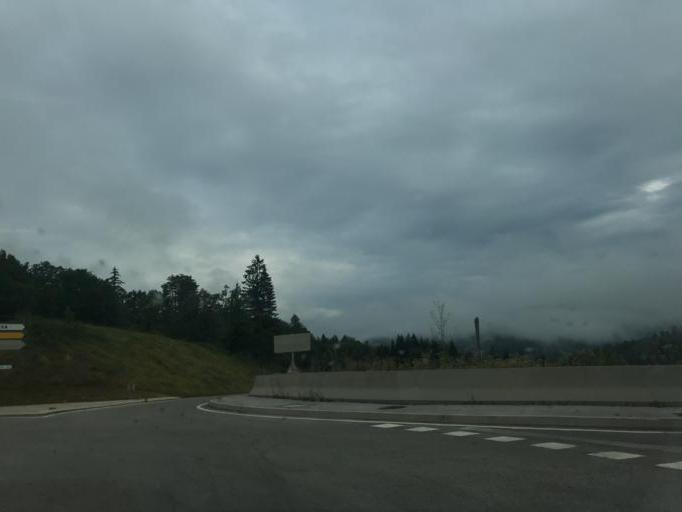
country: FR
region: Rhone-Alpes
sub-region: Departement de l'Ain
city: Dortan
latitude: 46.3062
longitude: 5.6621
